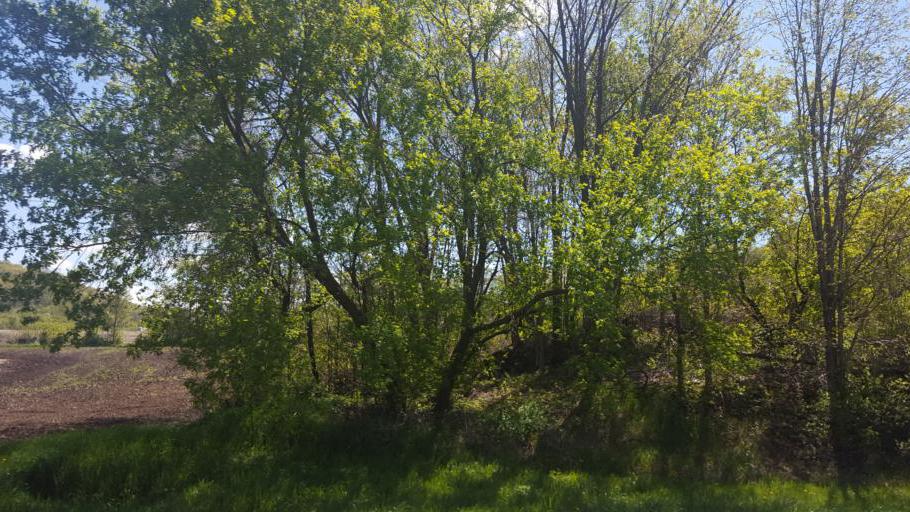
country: US
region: Wisconsin
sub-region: Vernon County
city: Hillsboro
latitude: 43.5628
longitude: -90.4180
